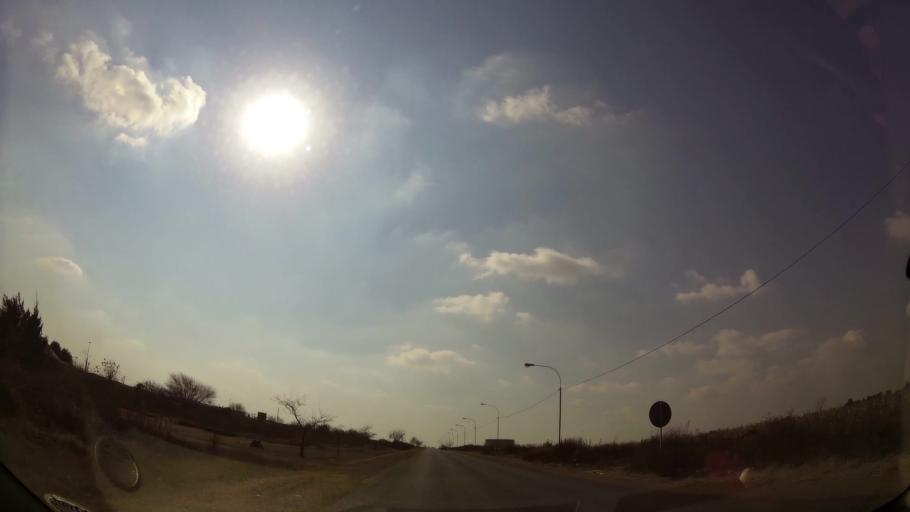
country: ZA
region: Gauteng
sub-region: Ekurhuleni Metropolitan Municipality
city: Springs
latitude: -26.1300
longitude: 28.4855
